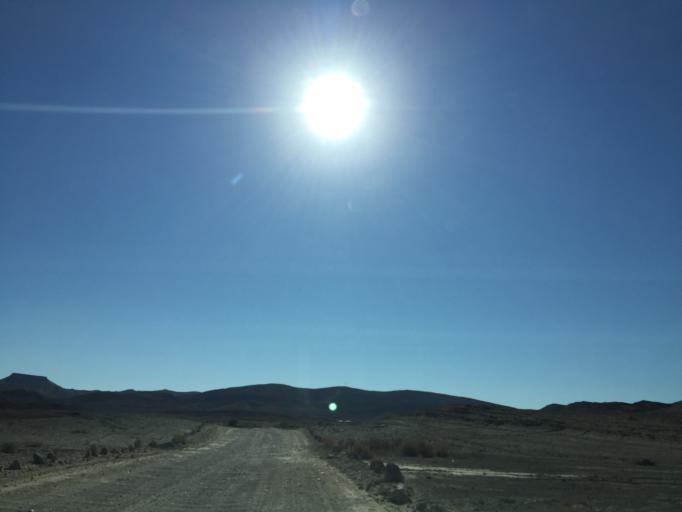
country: IL
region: Southern District
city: Mitzpe Ramon
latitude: 30.6040
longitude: 34.8971
